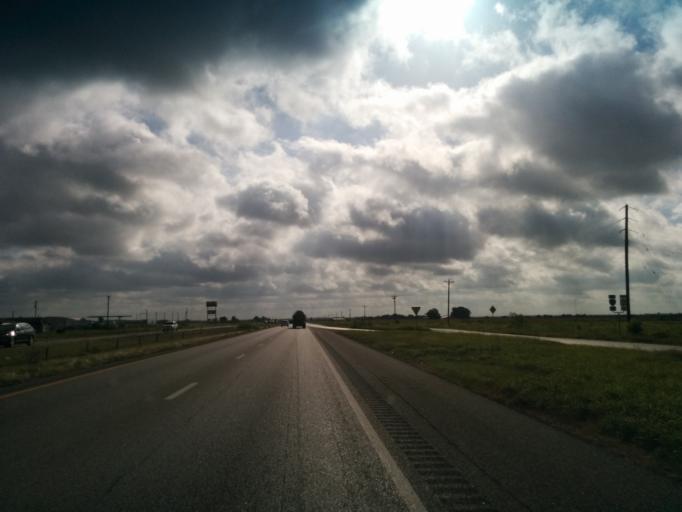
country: US
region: Texas
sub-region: Guadalupe County
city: Marion
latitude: 29.5193
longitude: -98.1377
